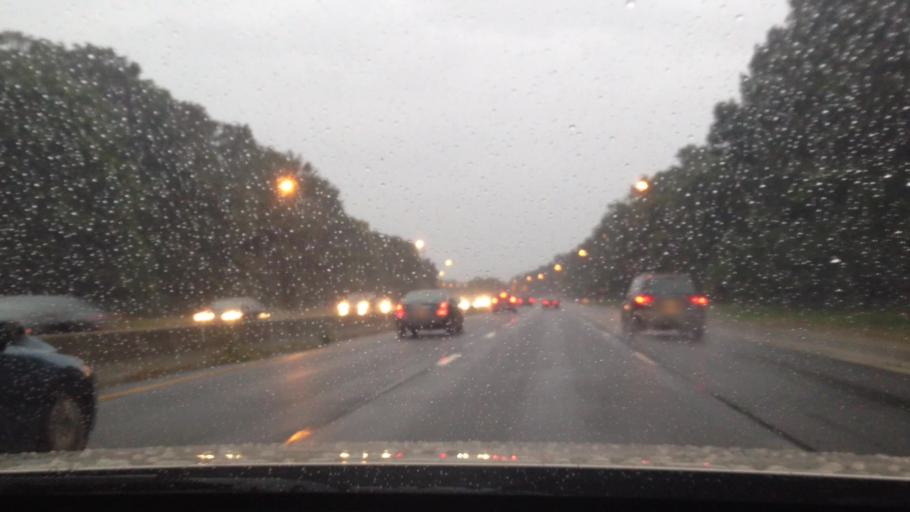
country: US
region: New York
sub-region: Suffolk County
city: West Babylon
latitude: 40.7285
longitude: -73.3693
